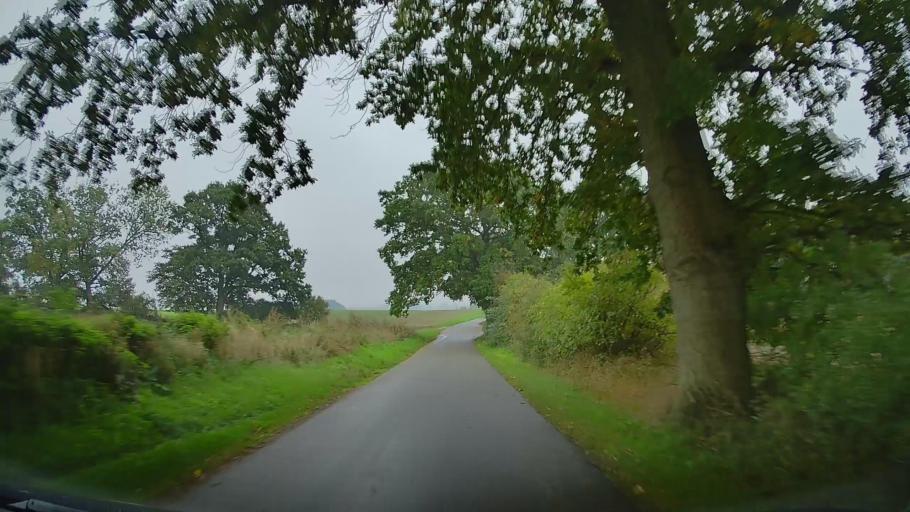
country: DE
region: Mecklenburg-Vorpommern
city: Gramkow
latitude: 53.9240
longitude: 11.3431
